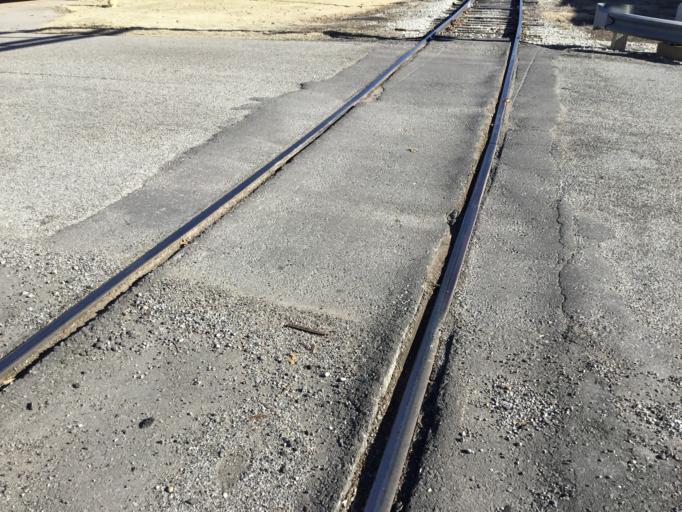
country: US
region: Kansas
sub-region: McPherson County
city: McPherson
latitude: 38.3725
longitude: -97.6630
